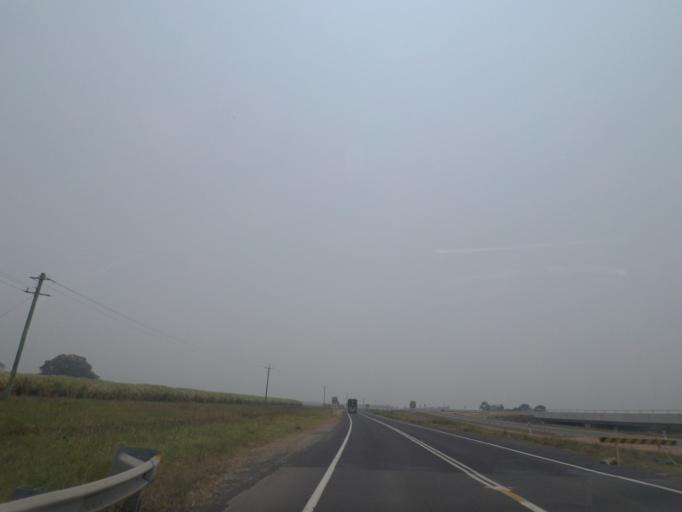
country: AU
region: New South Wales
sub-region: Clarence Valley
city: Maclean
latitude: -29.4168
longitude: 153.2411
